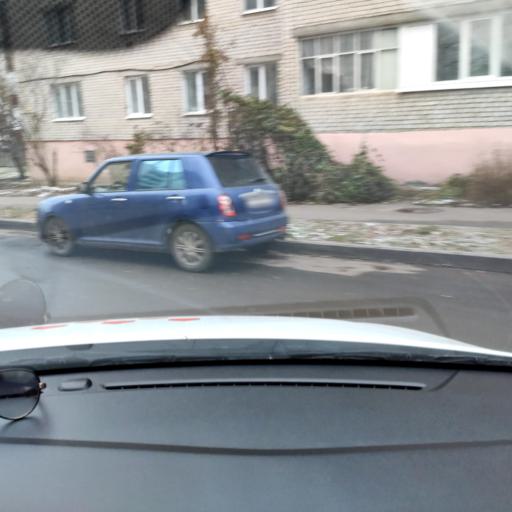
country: RU
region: Tatarstan
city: Vysokaya Gora
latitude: 55.8587
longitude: 49.2236
